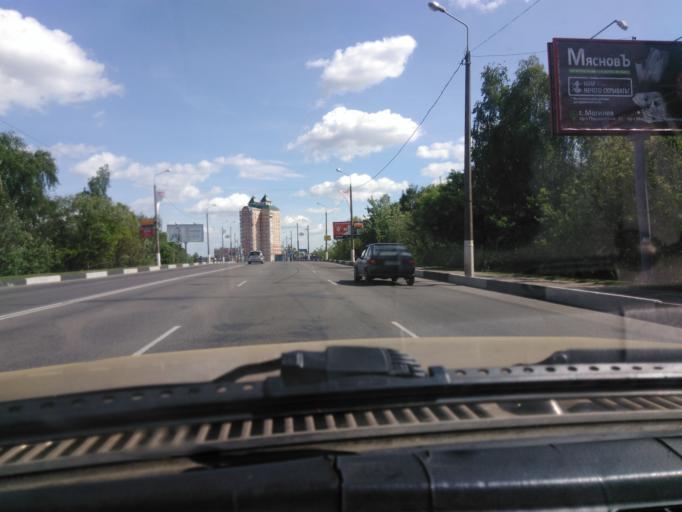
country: BY
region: Mogilev
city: Mahilyow
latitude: 53.9154
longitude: 30.3152
